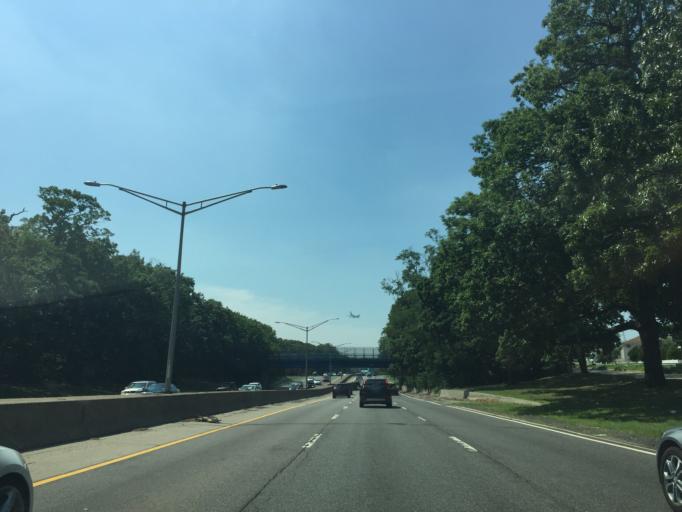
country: US
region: New York
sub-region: Nassau County
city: Bellerose Terrace
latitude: 40.7070
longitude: -73.7275
